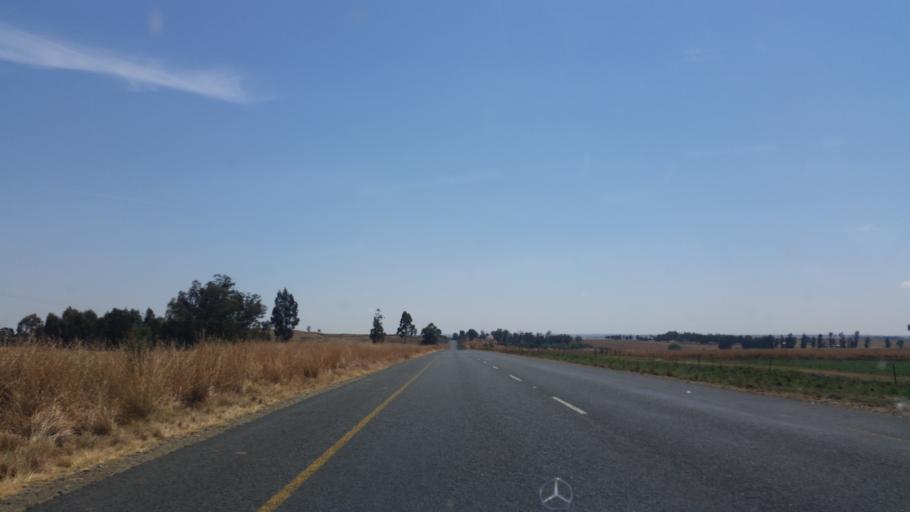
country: ZA
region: Orange Free State
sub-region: Thabo Mofutsanyana District Municipality
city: Phuthaditjhaba
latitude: -28.2390
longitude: 28.7083
